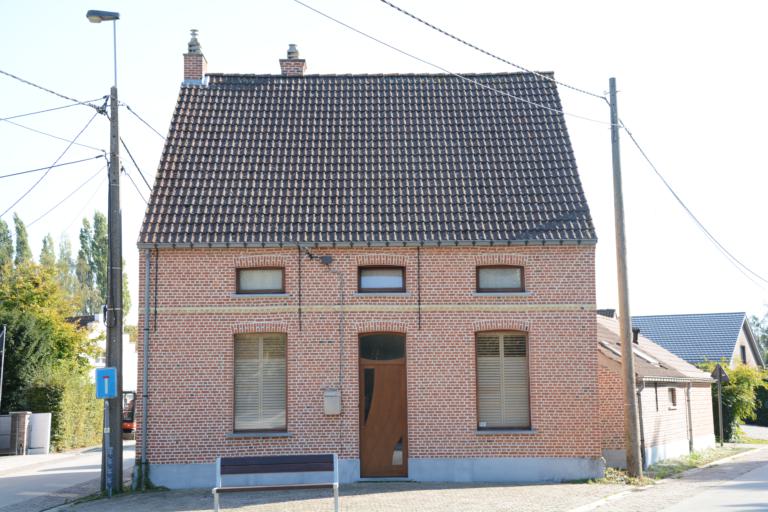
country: BE
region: Flanders
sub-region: Provincie Oost-Vlaanderen
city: Buggenhout
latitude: 51.0262
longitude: 4.2361
